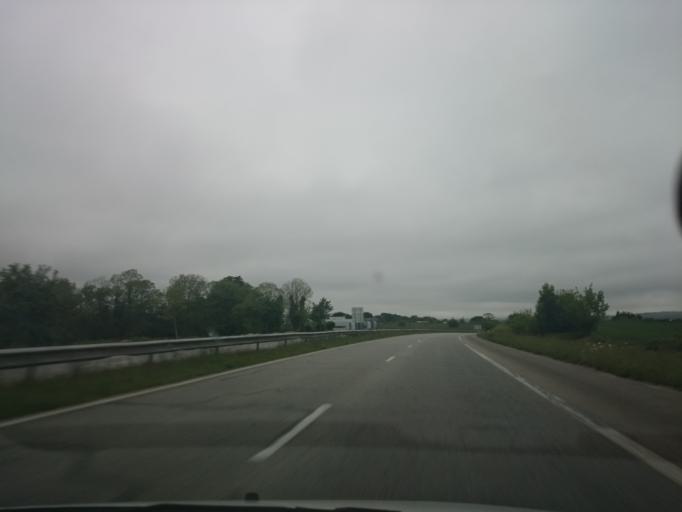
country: FR
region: Brittany
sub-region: Departement du Finistere
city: Ergue-Gaberic
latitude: 47.9838
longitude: -4.0187
